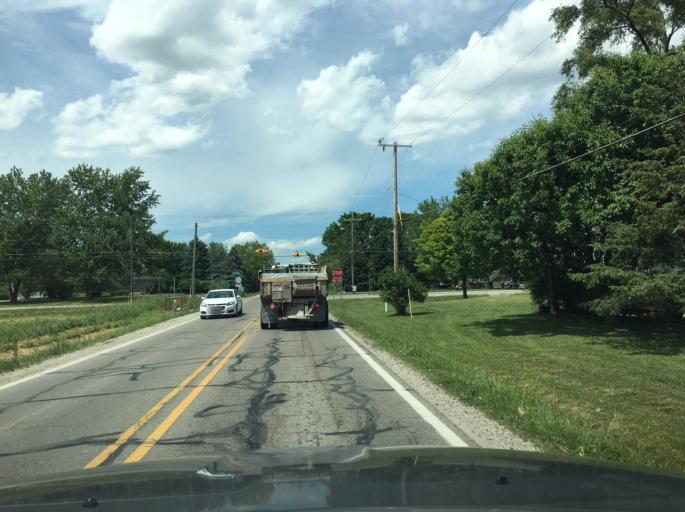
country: US
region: Michigan
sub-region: Macomb County
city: Romeo
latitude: 42.7596
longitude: -82.9610
